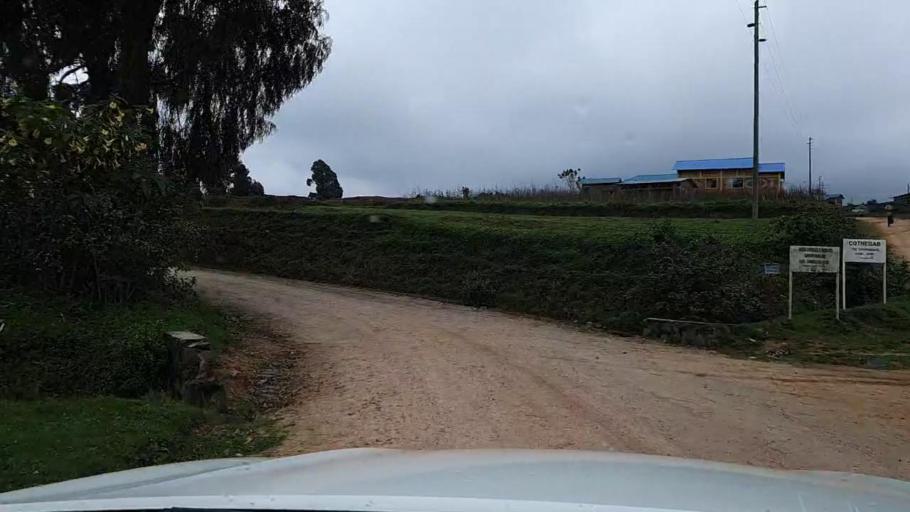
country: RW
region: Southern Province
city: Nzega
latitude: -2.3760
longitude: 29.3817
